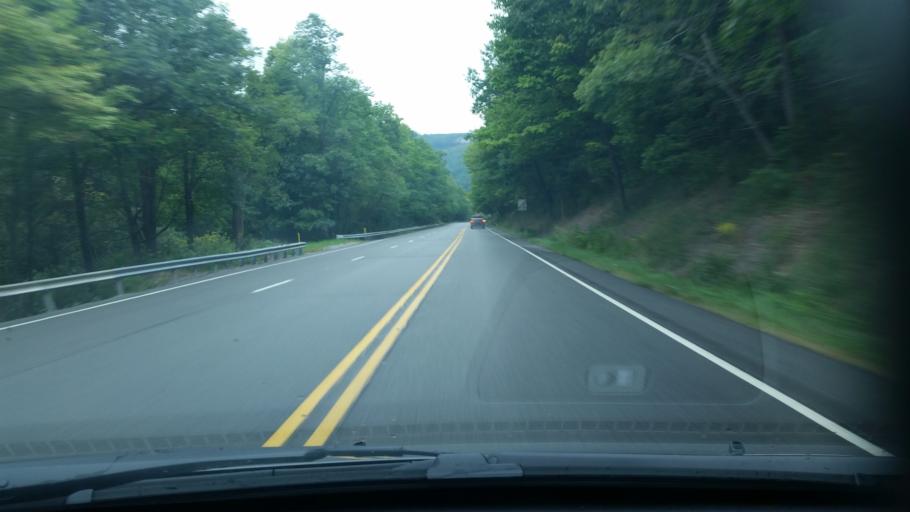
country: US
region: Pennsylvania
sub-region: Clearfield County
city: Shiloh
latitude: 41.0673
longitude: -78.3210
